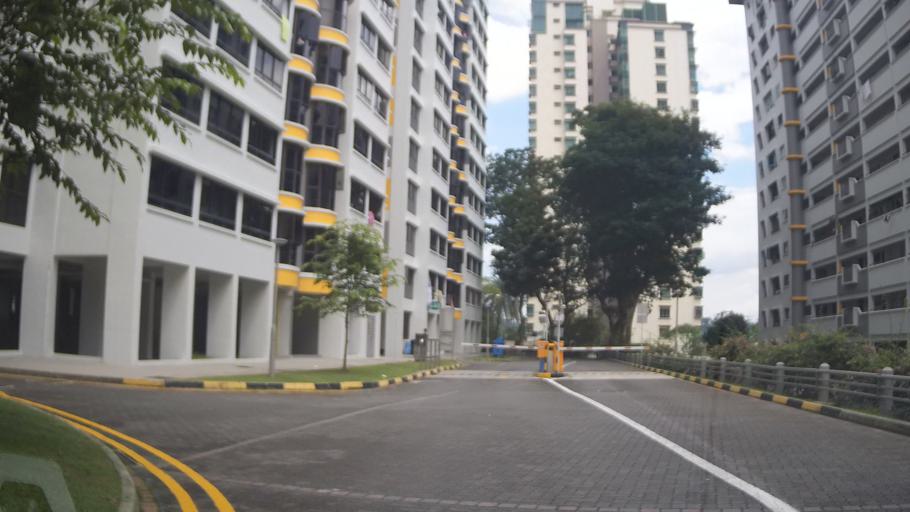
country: MY
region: Johor
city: Johor Bahru
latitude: 1.3975
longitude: 103.7491
